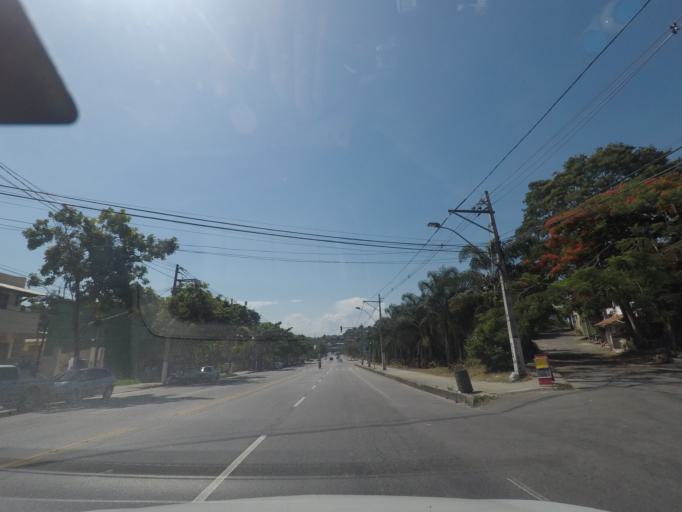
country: BR
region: Rio de Janeiro
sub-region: Niteroi
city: Niteroi
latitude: -22.9106
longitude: -43.0613
